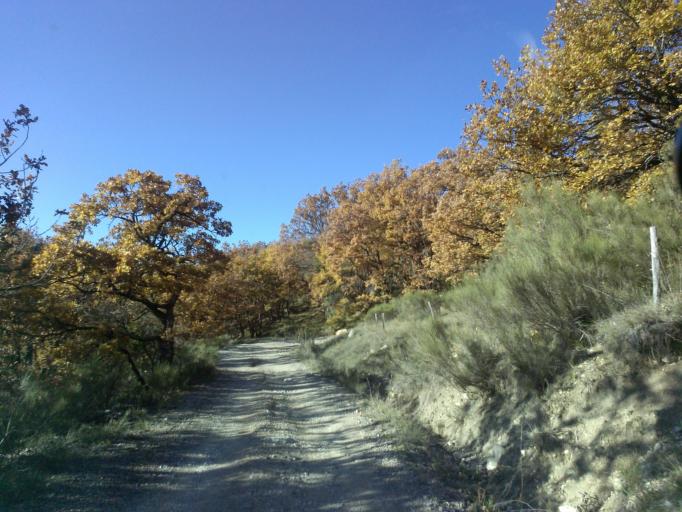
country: FR
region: Provence-Alpes-Cote d'Azur
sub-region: Departement des Alpes-de-Haute-Provence
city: Le Brusquet
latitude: 44.1896
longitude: 6.2597
